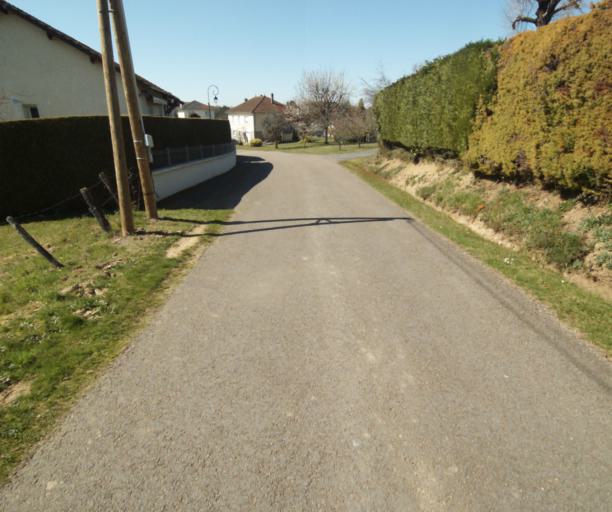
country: FR
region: Limousin
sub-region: Departement de la Correze
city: Saint-Mexant
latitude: 45.2793
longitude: 1.6626
